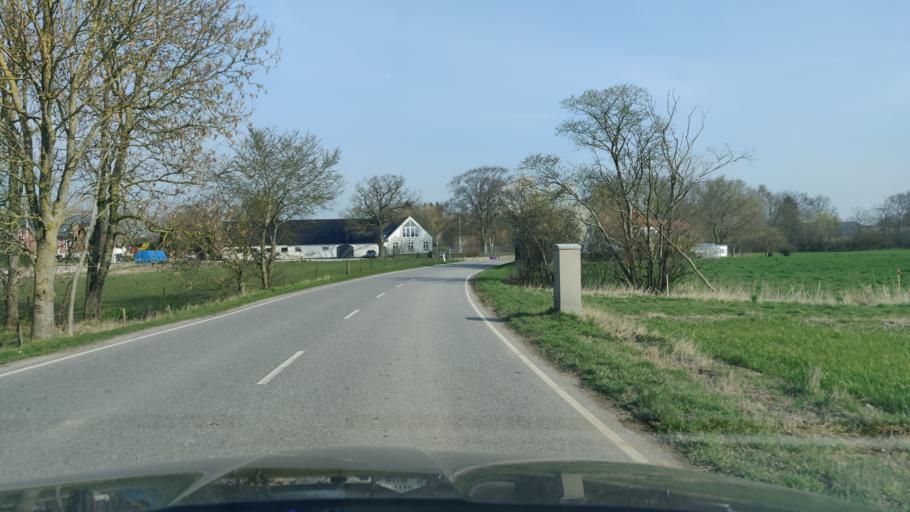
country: DK
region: South Denmark
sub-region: Nordfyns Kommune
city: Sonderso
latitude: 55.5102
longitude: 10.2498
